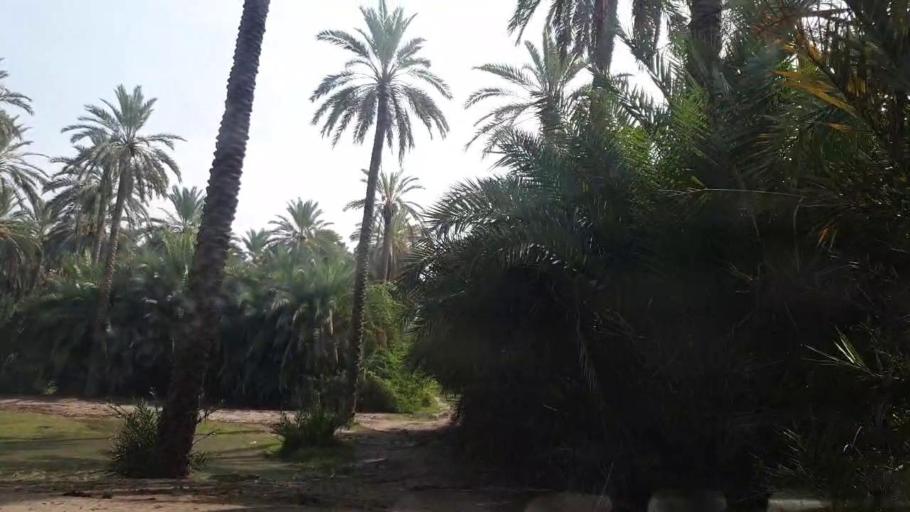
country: PK
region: Sindh
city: Khairpur
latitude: 27.5838
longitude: 68.7700
